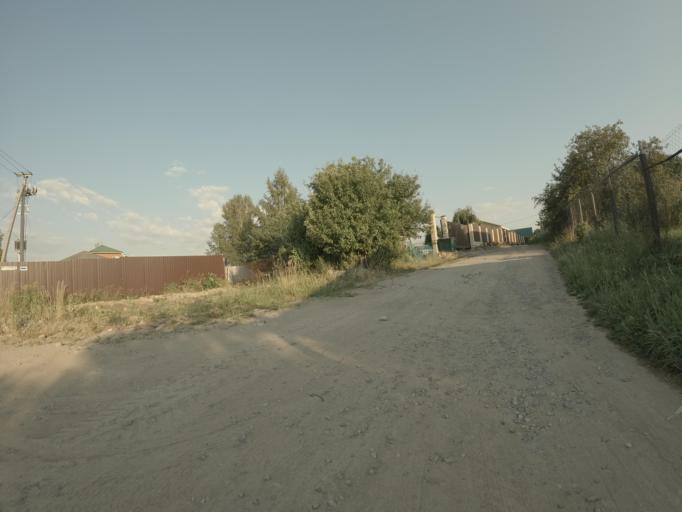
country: RU
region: Leningrad
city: Koltushi
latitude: 59.8905
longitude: 30.6979
